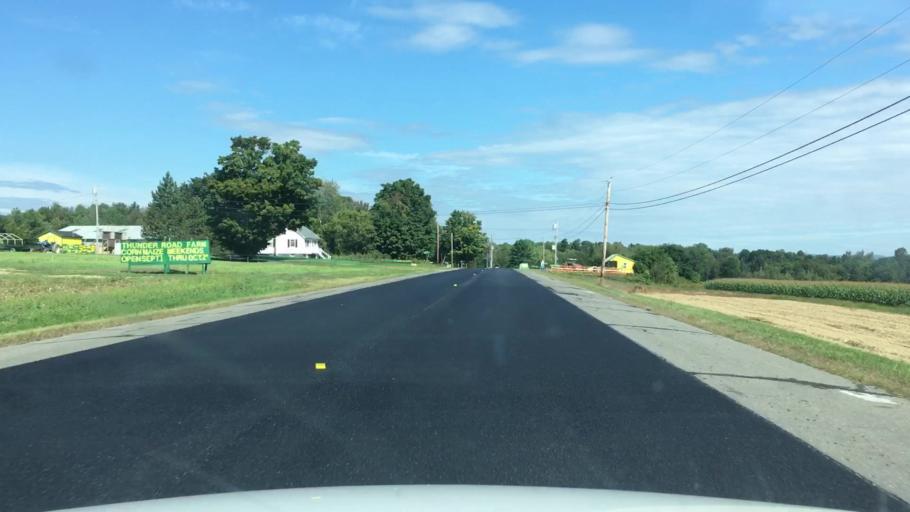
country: US
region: Maine
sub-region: Penobscot County
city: Corinna
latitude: 44.9071
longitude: -69.2645
